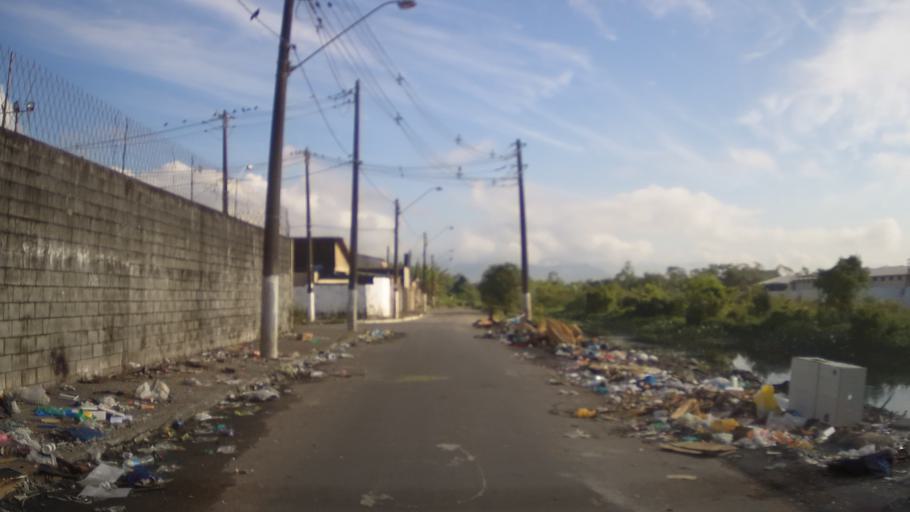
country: BR
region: Sao Paulo
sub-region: Praia Grande
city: Praia Grande
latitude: -24.0135
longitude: -46.4754
